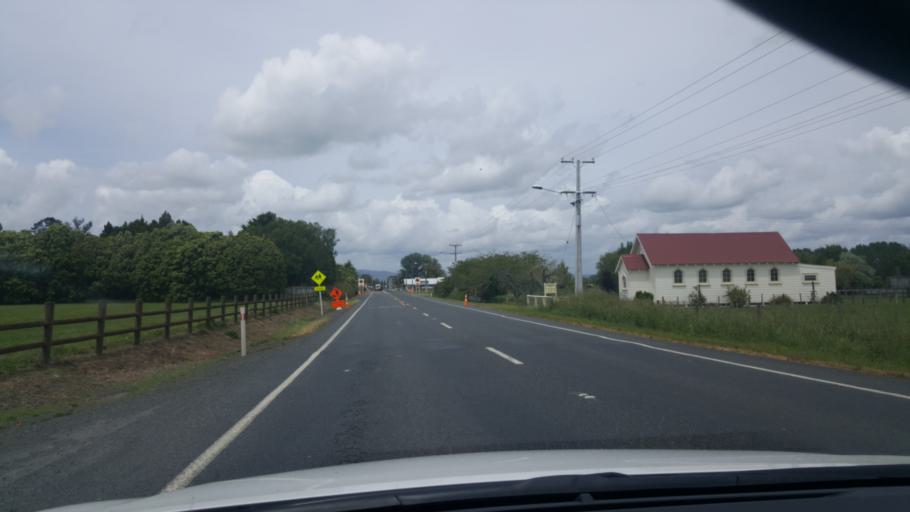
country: NZ
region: Waikato
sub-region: Matamata-Piako District
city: Matamata
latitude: -37.8801
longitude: 175.7562
